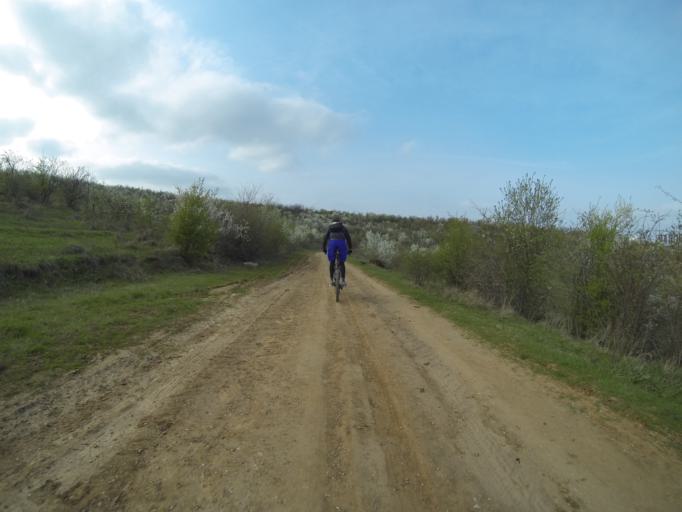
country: RO
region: Dolj
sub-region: Comuna Podari
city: Podari
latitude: 44.2466
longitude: 23.7672
